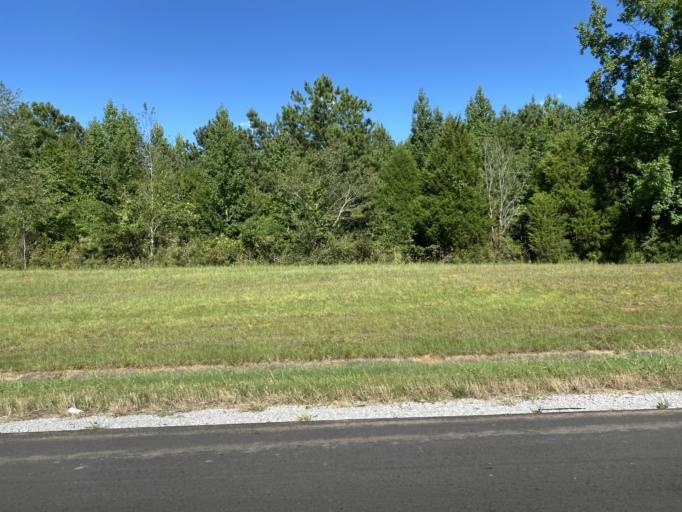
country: US
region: Alabama
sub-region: Limestone County
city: Athens
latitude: 34.7518
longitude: -86.9381
